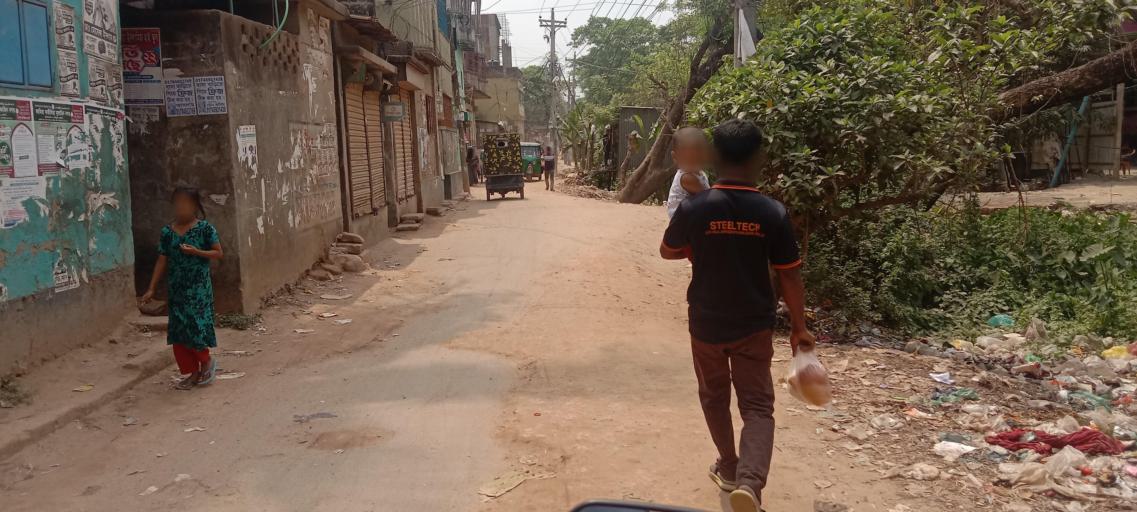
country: BD
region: Dhaka
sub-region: Dhaka
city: Dhaka
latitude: 23.6777
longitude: 90.4199
